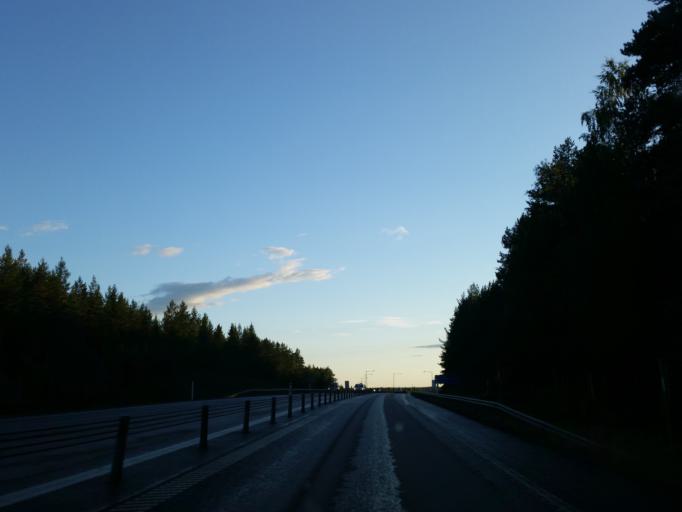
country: SE
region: Vaesterbotten
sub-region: Umea Kommun
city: Saevar
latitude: 63.9023
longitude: 20.5739
